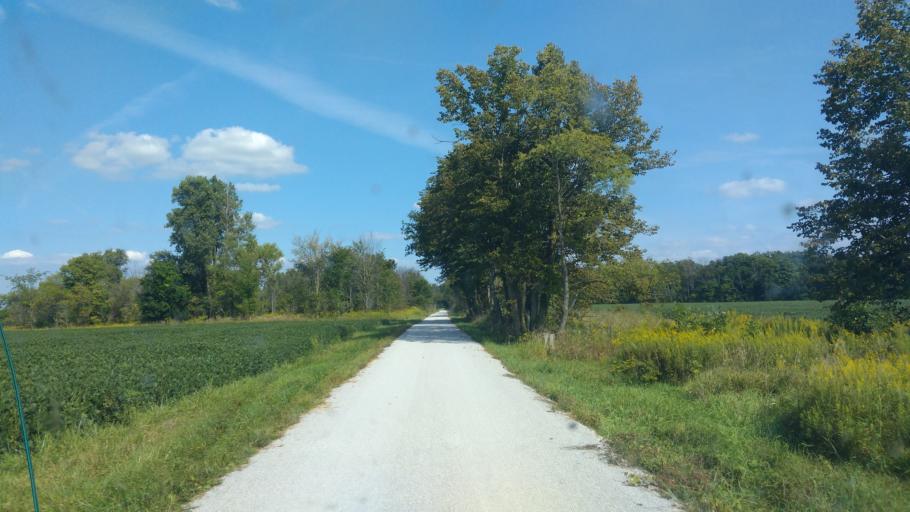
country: US
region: Ohio
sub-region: Hardin County
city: Kenton
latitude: 40.6293
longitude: -83.4477
